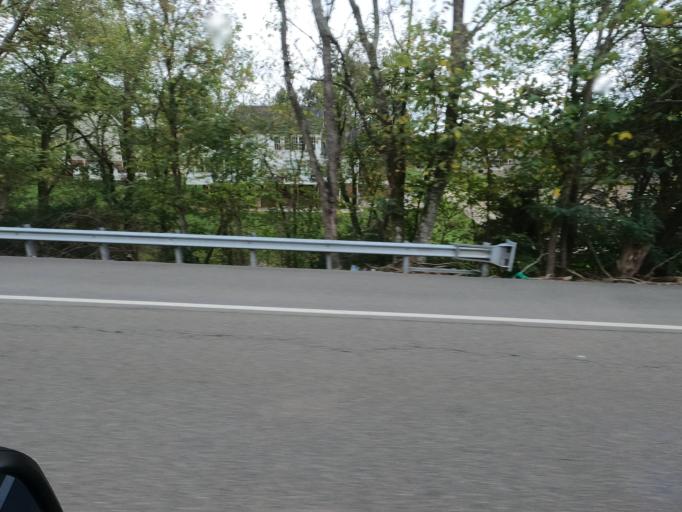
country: US
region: Tennessee
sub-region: Sullivan County
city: Kingsport
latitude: 36.5552
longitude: -82.6087
